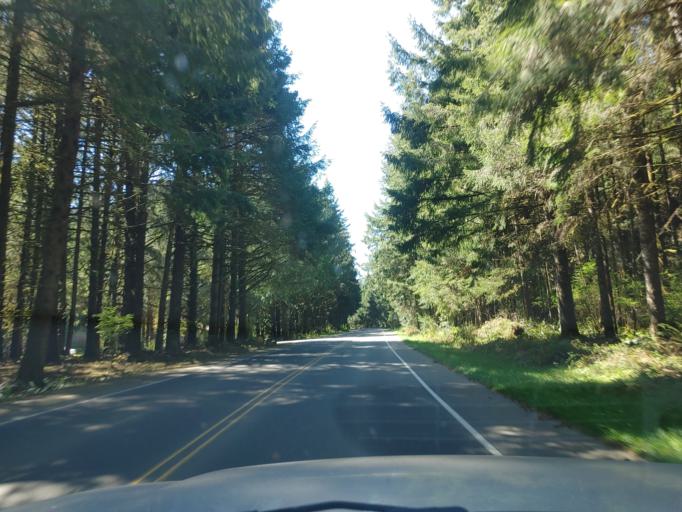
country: US
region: Oregon
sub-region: Clatsop County
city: Warrenton
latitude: 46.1377
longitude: -123.8778
